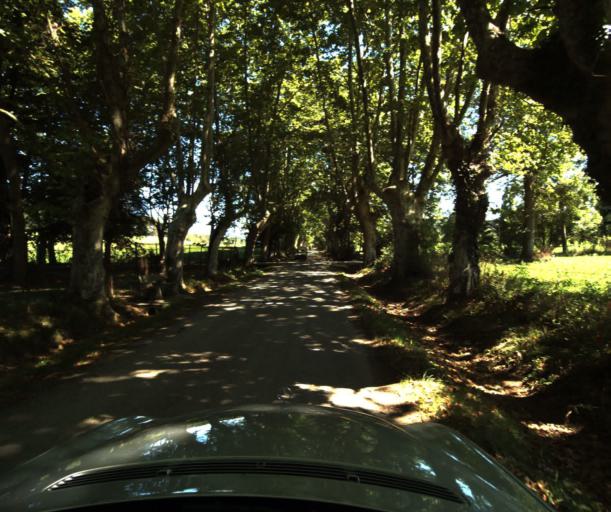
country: FR
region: Midi-Pyrenees
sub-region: Departement de l'Ariege
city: Lavelanet
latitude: 42.9919
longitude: 1.9131
